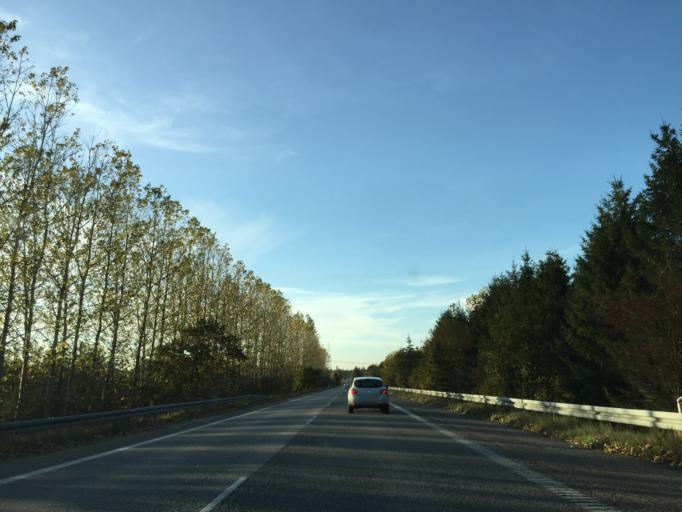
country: DK
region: South Denmark
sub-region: Aabenraa Kommune
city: Krusa
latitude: 54.8716
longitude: 9.3897
